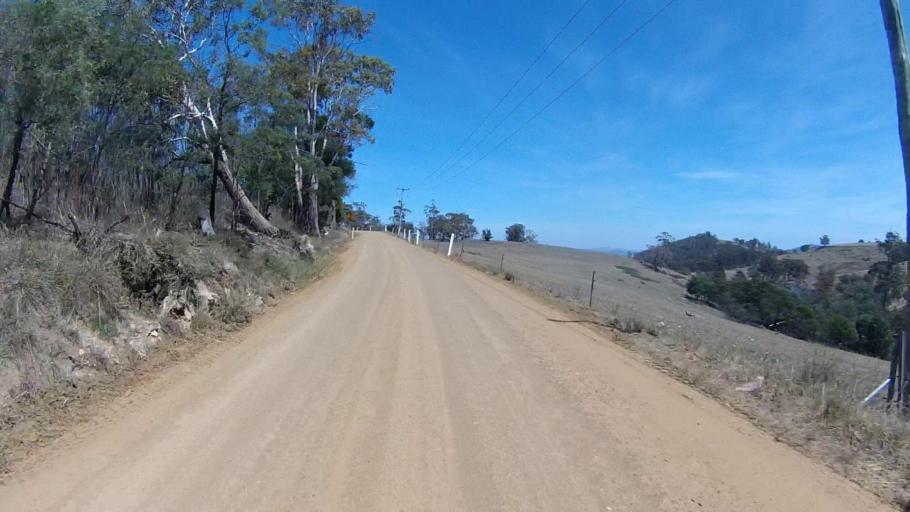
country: AU
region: Tasmania
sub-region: Sorell
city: Sorell
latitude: -42.7809
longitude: 147.6467
